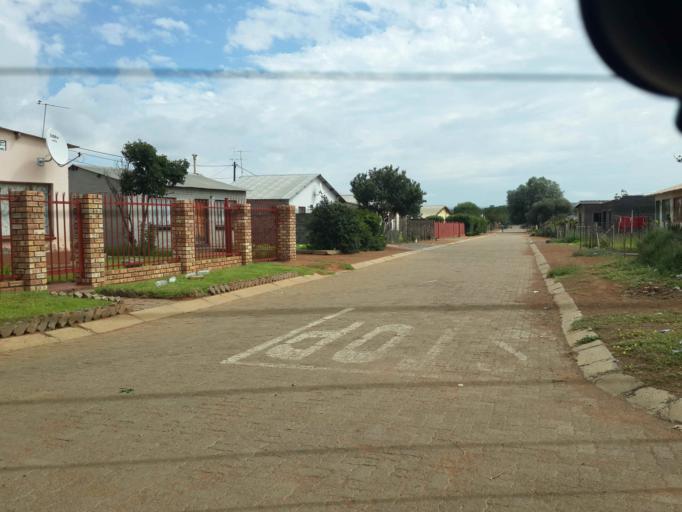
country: ZA
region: Northern Cape
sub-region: Siyanda District Municipality
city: Danielskuil
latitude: -28.1999
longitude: 23.5569
